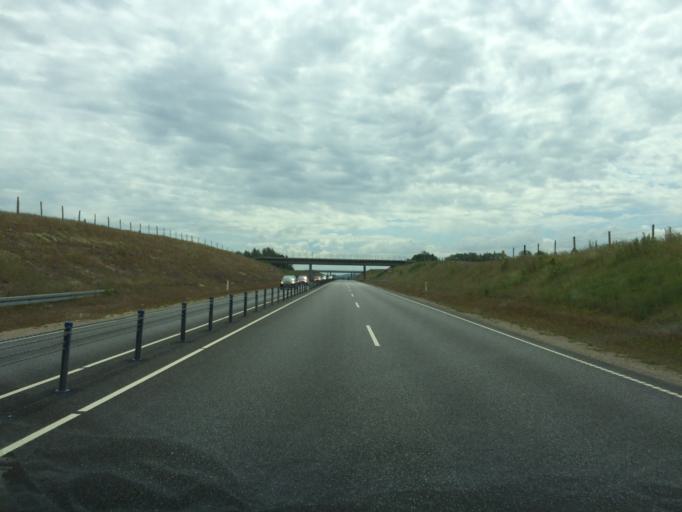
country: DK
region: Zealand
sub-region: Odsherred Kommune
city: Hojby
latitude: 55.8631
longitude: 11.5918
